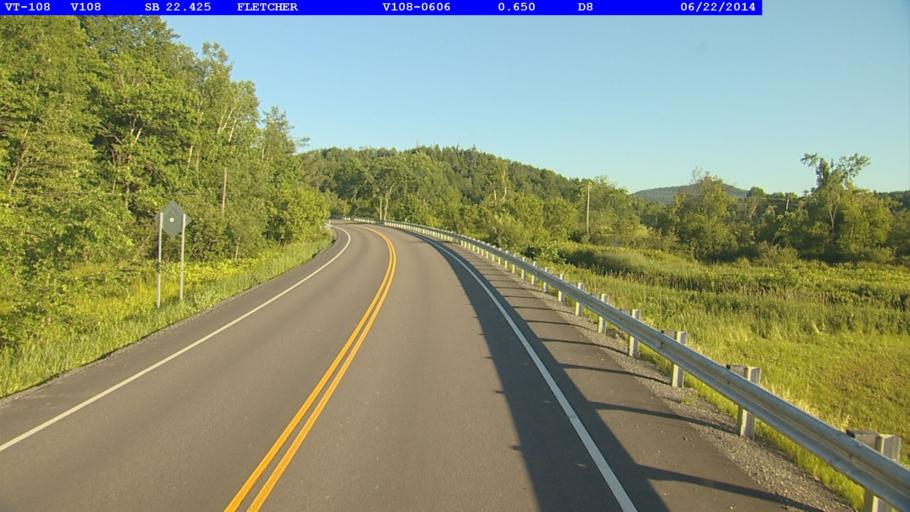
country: US
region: Vermont
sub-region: Lamoille County
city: Johnson
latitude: 44.7113
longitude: -72.8384
